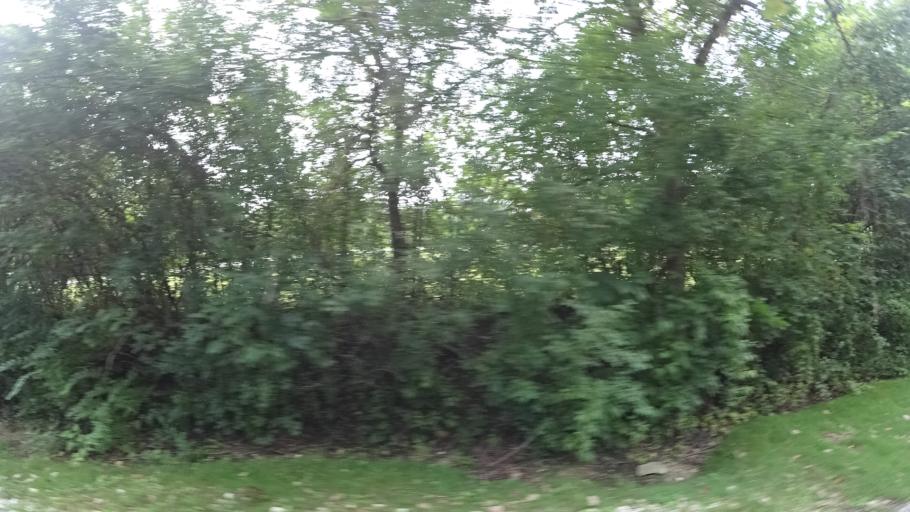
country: US
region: Illinois
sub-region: Will County
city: Goodings Grove
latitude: 41.6566
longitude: -87.8980
